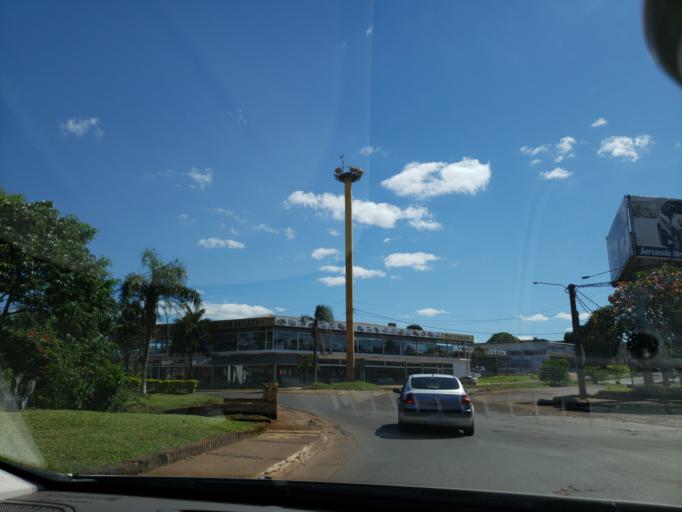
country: AR
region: Misiones
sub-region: Departamento de Capital
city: Posadas
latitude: -27.4041
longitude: -55.9028
